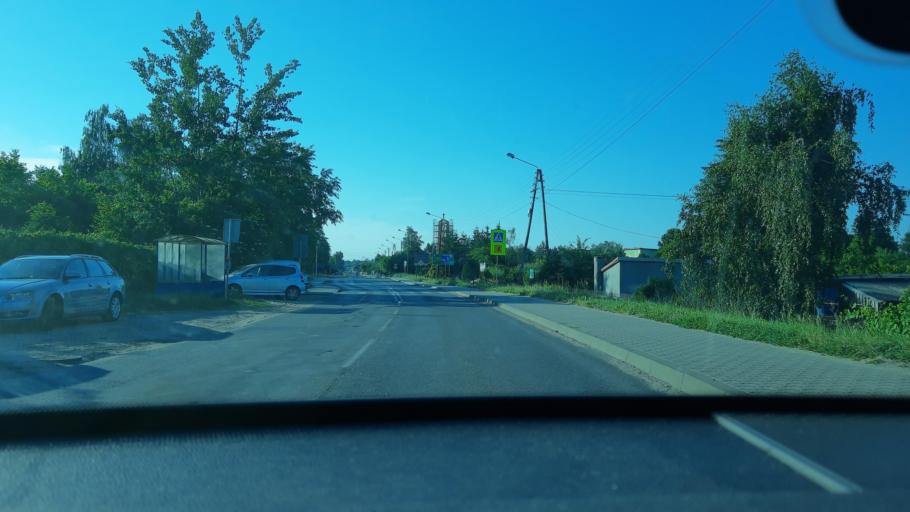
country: PL
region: Lodz Voivodeship
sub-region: Powiat sieradzki
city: Sieradz
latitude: 51.5754
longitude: 18.7467
